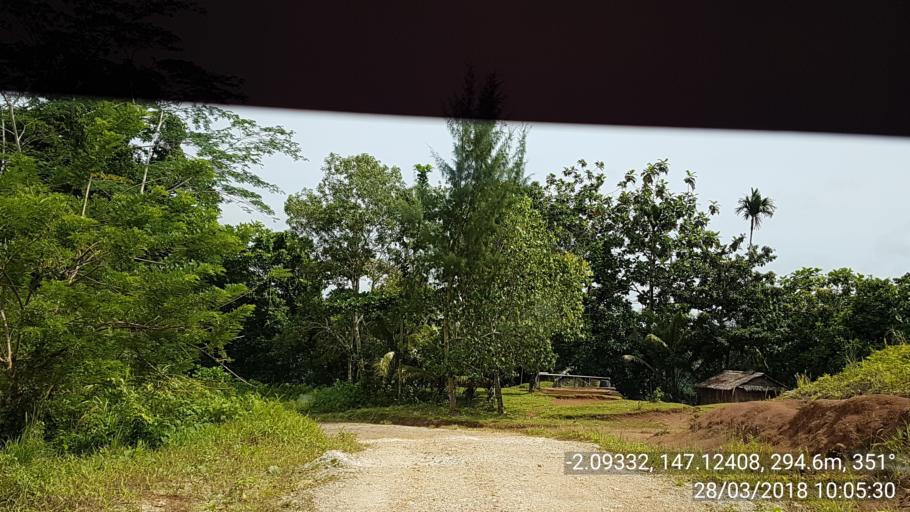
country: PG
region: Manus
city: Lorengau
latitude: -2.0933
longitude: 147.1242
